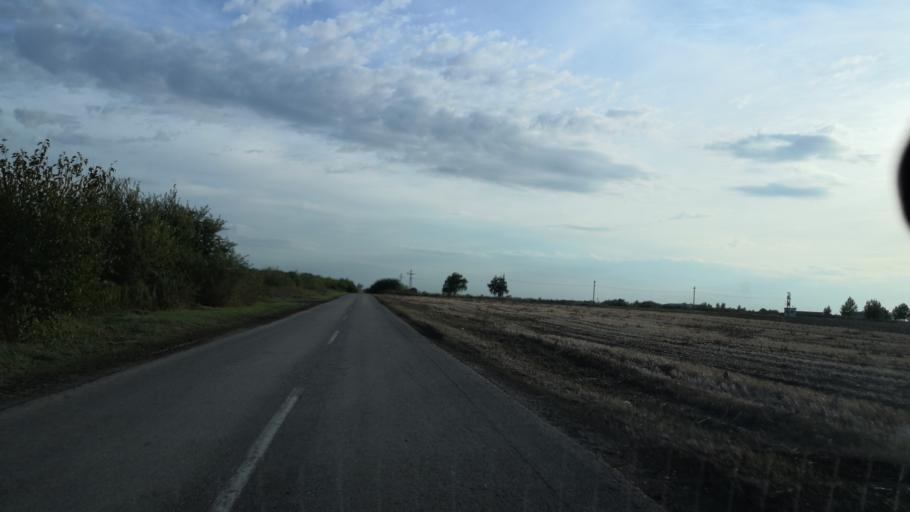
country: RS
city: Novi Karlovci
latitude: 45.0339
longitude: 20.1730
